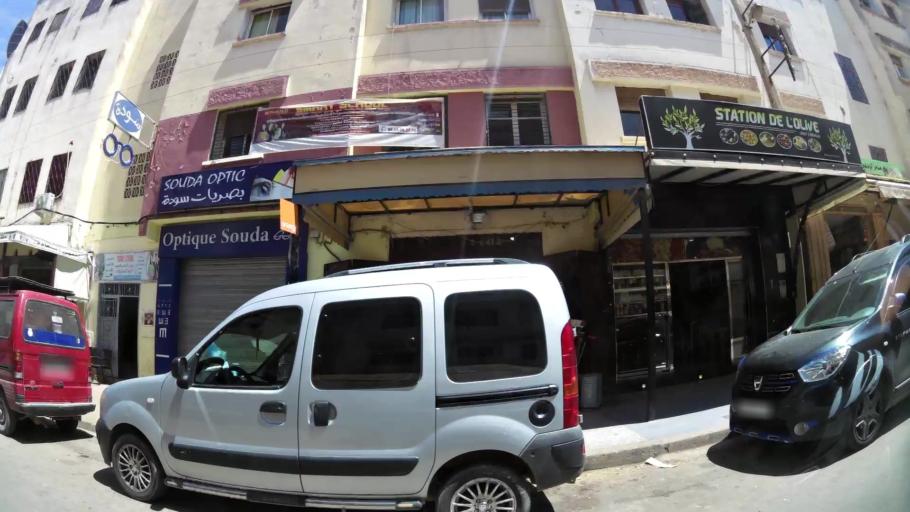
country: MA
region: Fes-Boulemane
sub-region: Fes
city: Fes
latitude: 34.0128
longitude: -4.9865
